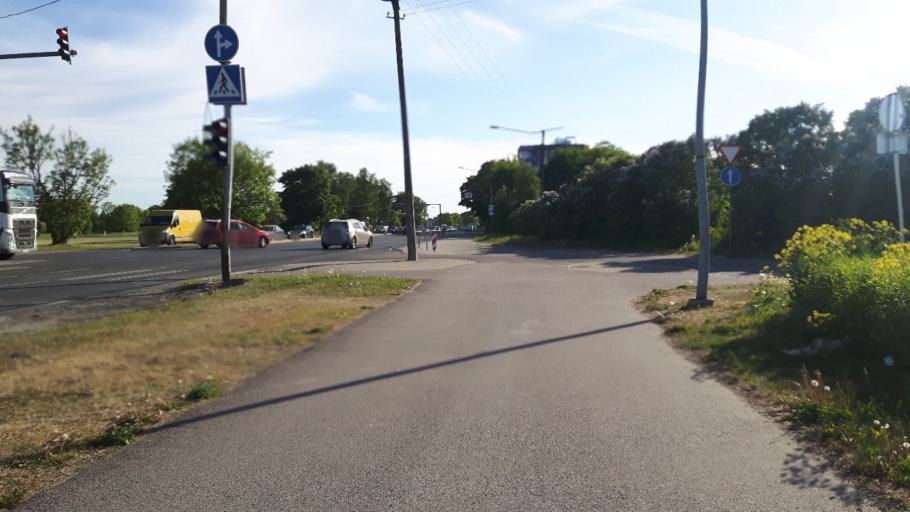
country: EE
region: Harju
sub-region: Viimsi vald
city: Viimsi
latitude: 59.4465
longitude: 24.8194
